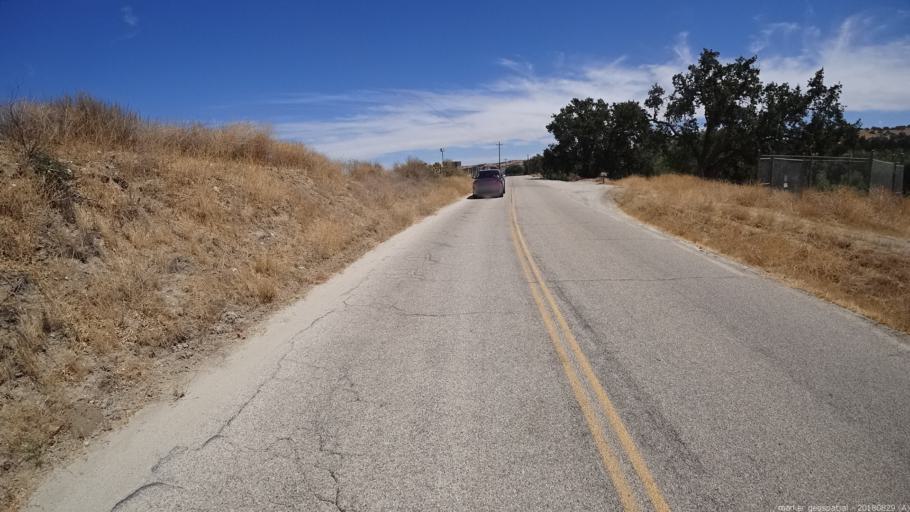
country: US
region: California
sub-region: San Luis Obispo County
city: Lake Nacimiento
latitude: 35.8093
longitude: -120.8553
